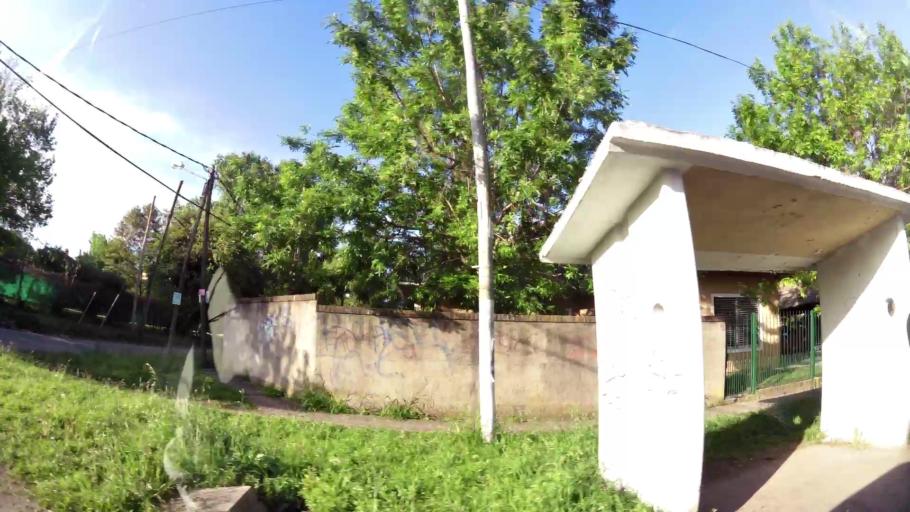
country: AR
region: Buenos Aires
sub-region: Partido de Quilmes
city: Quilmes
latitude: -34.7902
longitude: -58.2103
